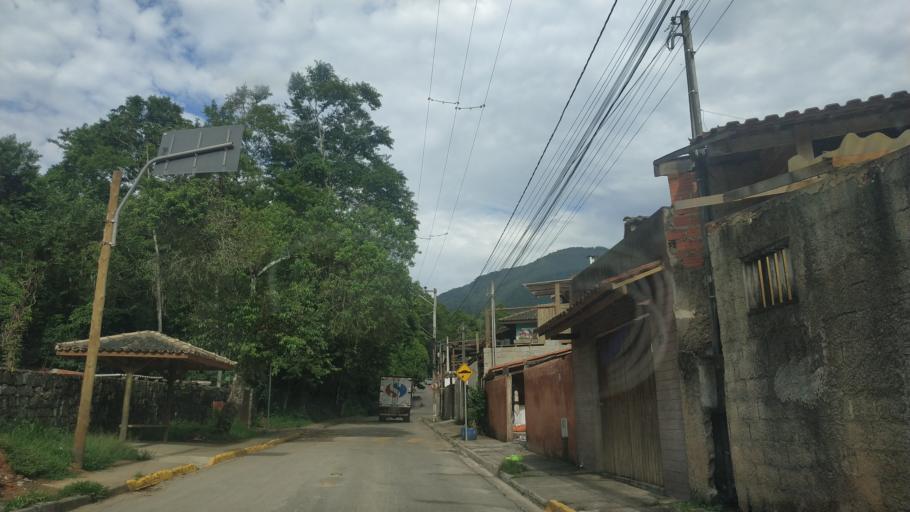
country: BR
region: Sao Paulo
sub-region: Ilhabela
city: Ilhabela
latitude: -23.8269
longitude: -45.3501
